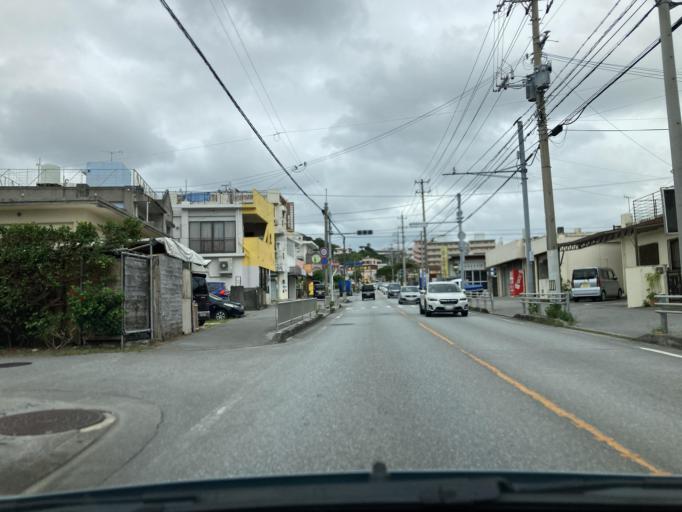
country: JP
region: Okinawa
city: Ginowan
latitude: 26.2310
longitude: 127.7532
